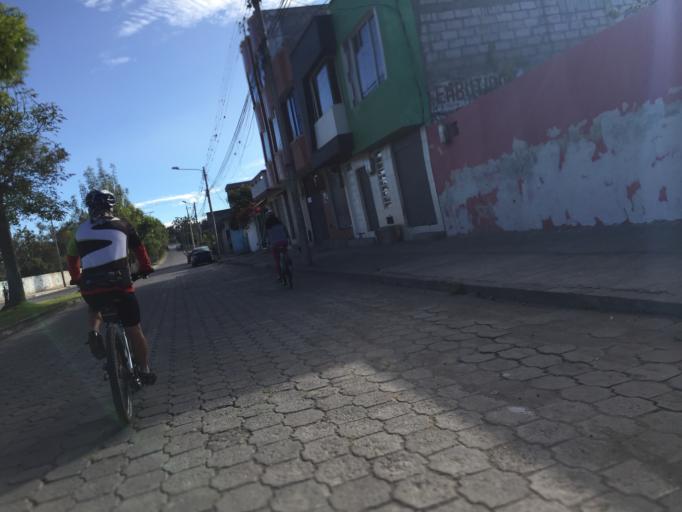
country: EC
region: Imbabura
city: Atuntaqui
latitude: 0.3373
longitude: -78.2090
